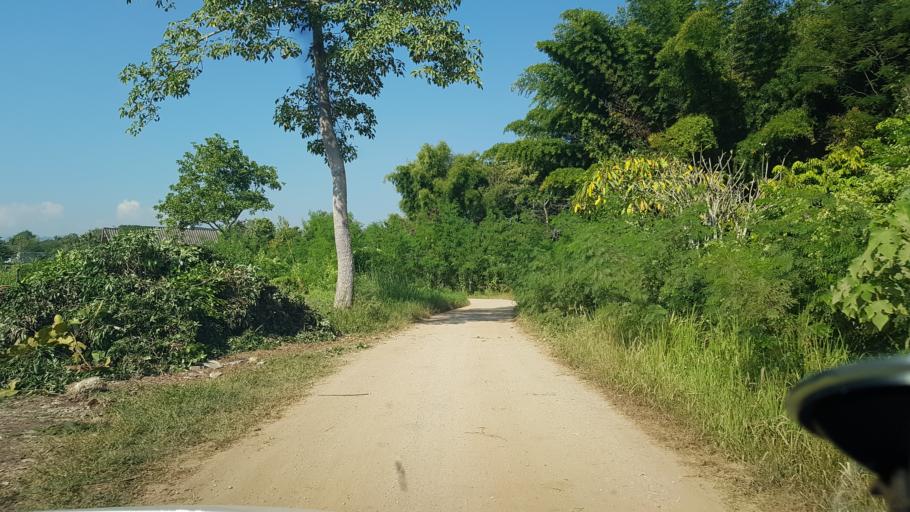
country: TH
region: Chiang Rai
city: Chiang Rai
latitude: 19.9018
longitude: 99.7946
